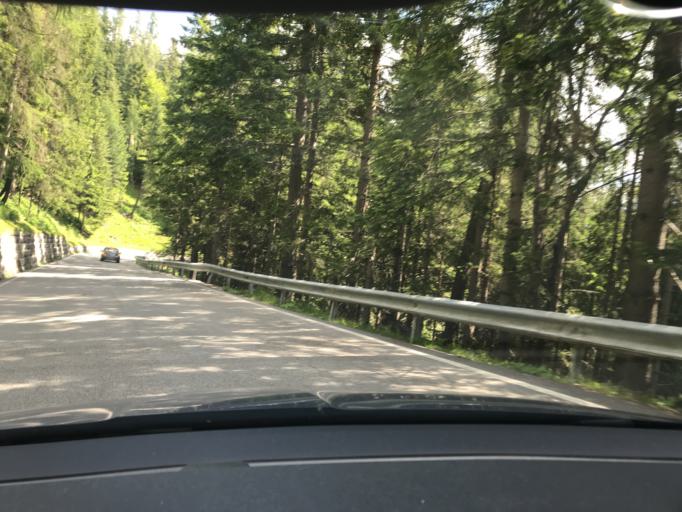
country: IT
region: Veneto
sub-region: Provincia di Belluno
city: Cortina d'Ampezzo
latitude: 46.5204
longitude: 12.1144
